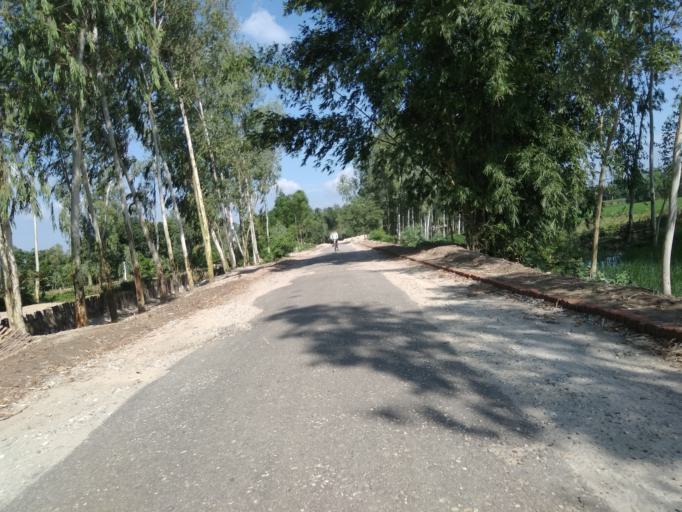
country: BD
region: Rangpur Division
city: Panchagarh
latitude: 26.2551
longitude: 88.6214
